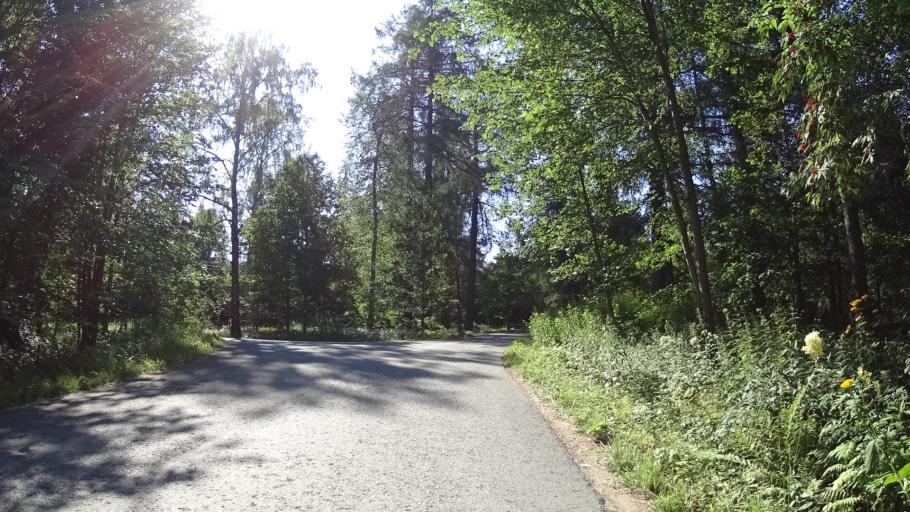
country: FI
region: Haeme
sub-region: Haemeenlinna
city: Haemeenlinna
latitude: 61.0265
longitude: 24.4485
